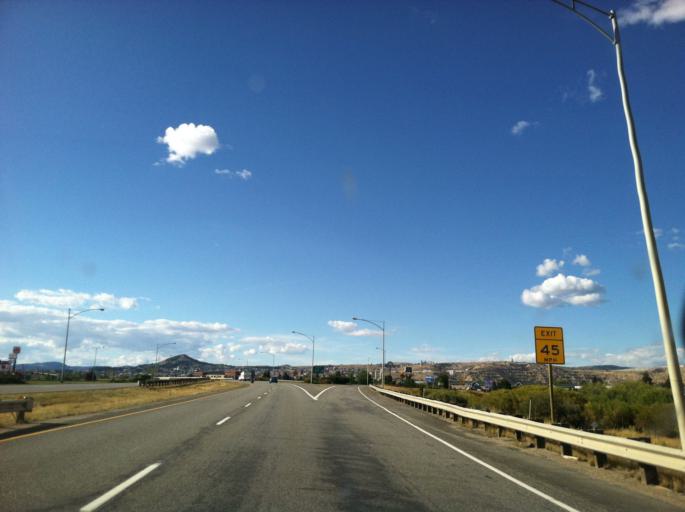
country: US
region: Montana
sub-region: Silver Bow County
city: Butte
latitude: 45.9829
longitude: -112.5056
